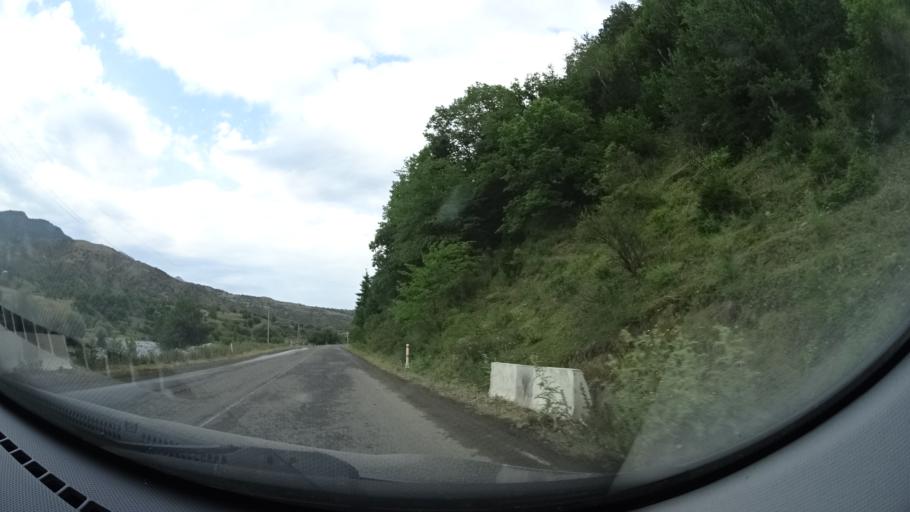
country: GE
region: Samtskhe-Javakheti
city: Adigeni
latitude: 41.6796
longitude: 42.6714
